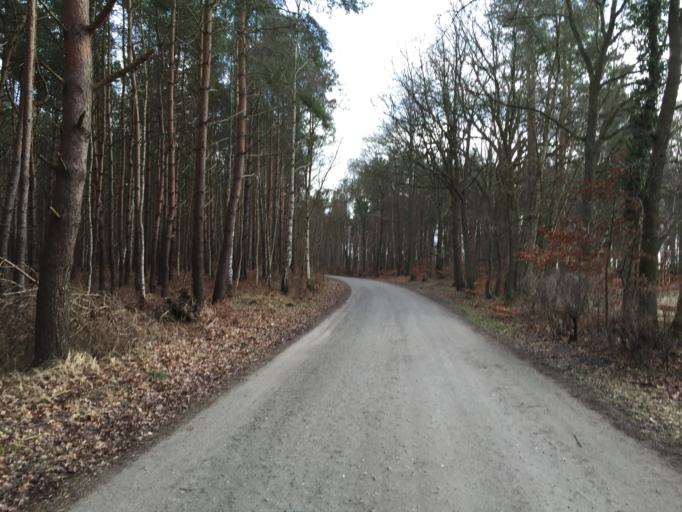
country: DE
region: Mecklenburg-Vorpommern
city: Rovershagen
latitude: 54.1851
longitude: 12.2394
